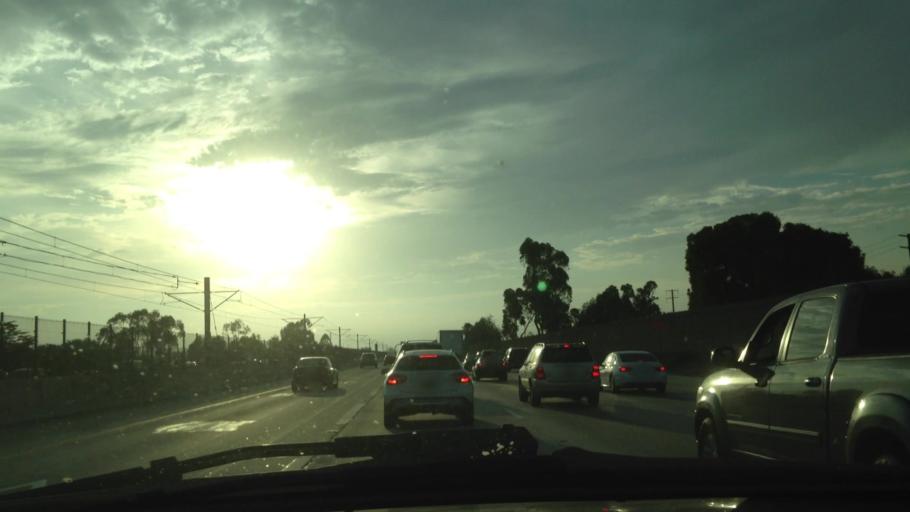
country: US
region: California
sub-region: Los Angeles County
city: Lynwood
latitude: 33.9181
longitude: -118.1974
